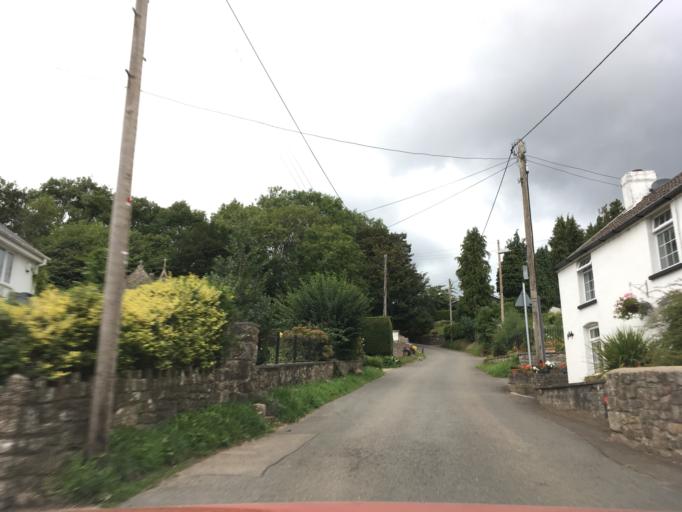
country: GB
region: Wales
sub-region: Newport
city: Llanvaches
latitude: 51.6278
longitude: -2.8004
